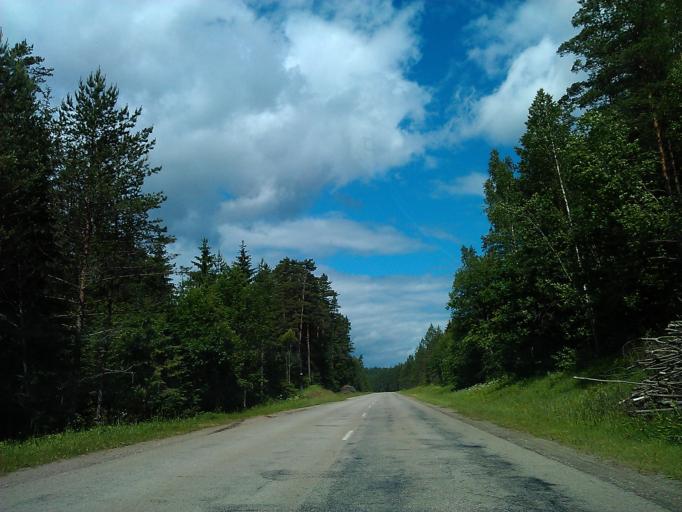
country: LV
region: Talsu Rajons
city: Sabile
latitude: 57.0741
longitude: 22.5328
